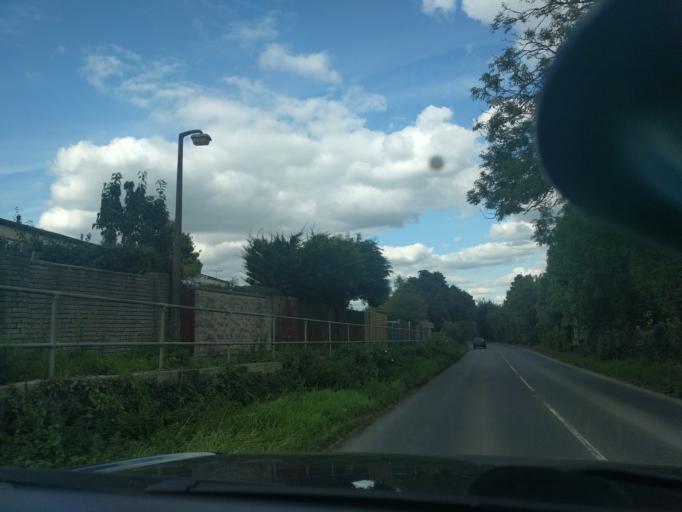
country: GB
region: England
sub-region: Wiltshire
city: Box
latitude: 51.4242
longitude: -2.2243
